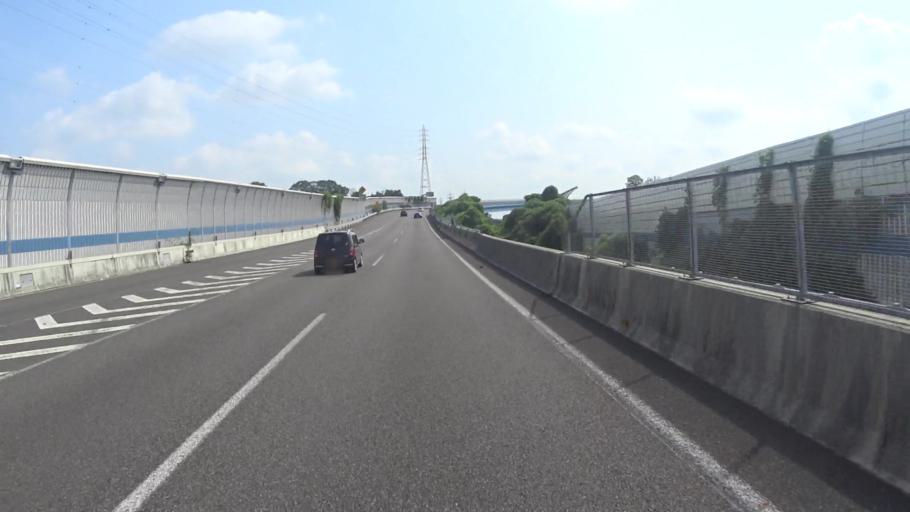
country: JP
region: Shiga Prefecture
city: Kusatsu
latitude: 34.9808
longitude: 135.9528
